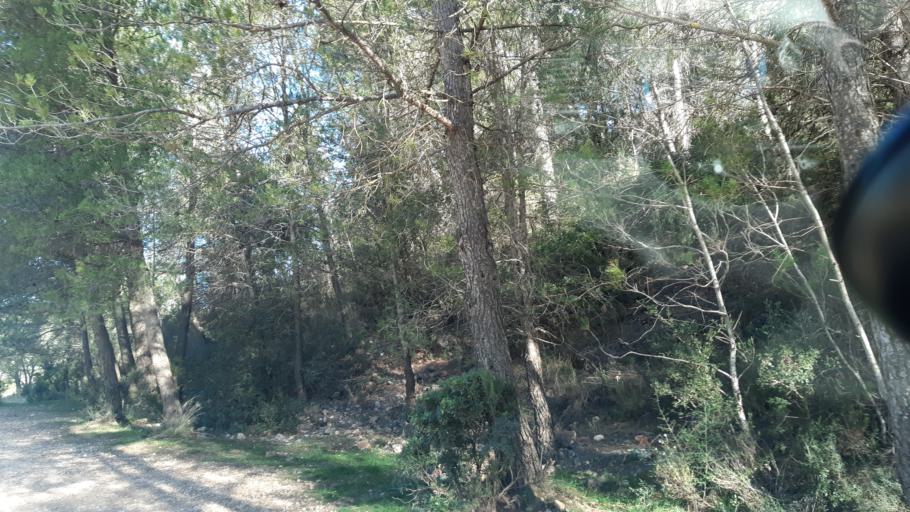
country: ES
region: Aragon
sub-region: Provincia de Teruel
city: Valderrobres
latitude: 40.8560
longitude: 0.2522
